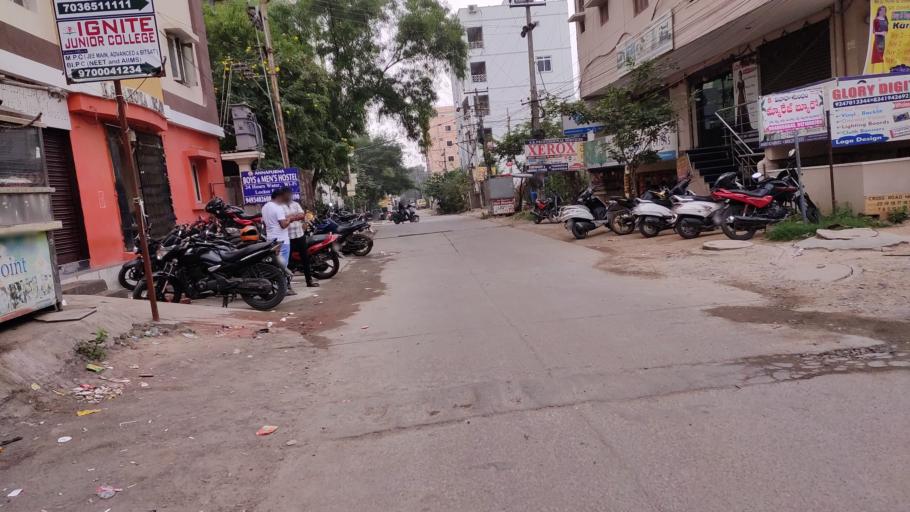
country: IN
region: Telangana
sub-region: Rangareddi
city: Kukatpalli
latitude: 17.4976
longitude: 78.3911
